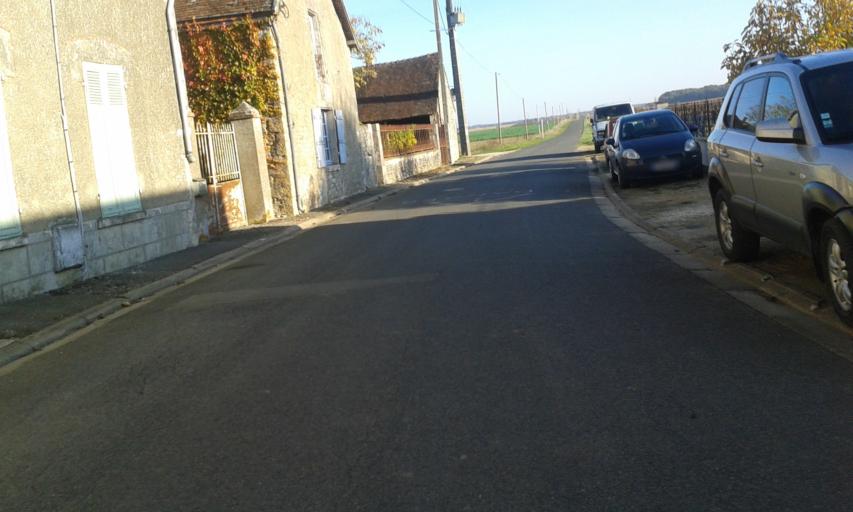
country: FR
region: Centre
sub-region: Departement du Loir-et-Cher
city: Ouzouer-le-Marche
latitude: 47.8775
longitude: 1.4218
